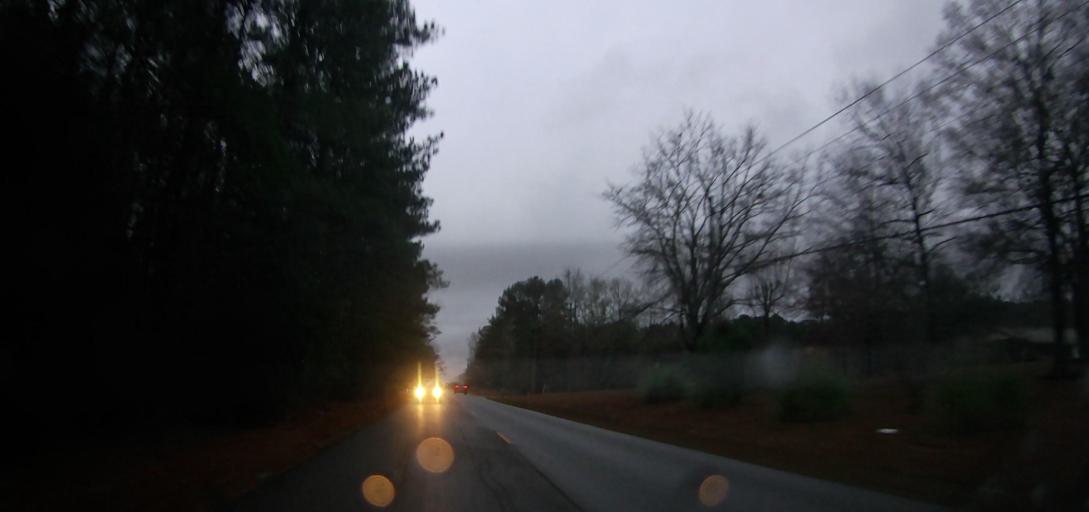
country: US
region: Alabama
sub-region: Tuscaloosa County
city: Vance
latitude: 33.1523
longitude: -87.2299
